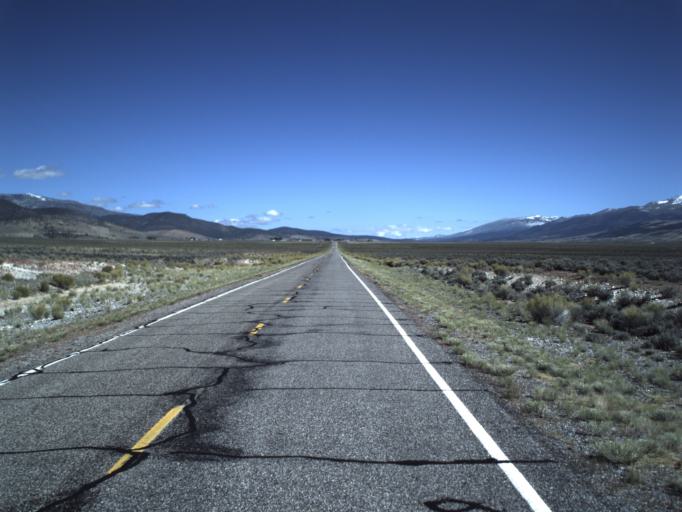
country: US
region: Utah
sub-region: Wayne County
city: Loa
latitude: 38.3931
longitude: -111.9319
